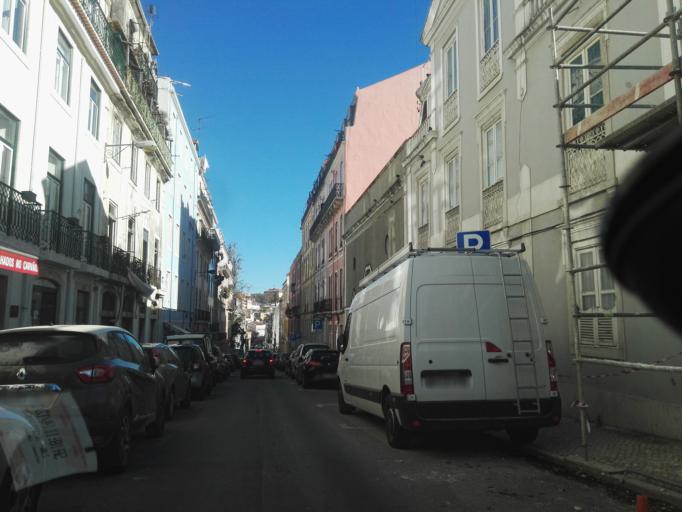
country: PT
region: Setubal
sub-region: Almada
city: Cacilhas
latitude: 38.7075
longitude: -9.1560
